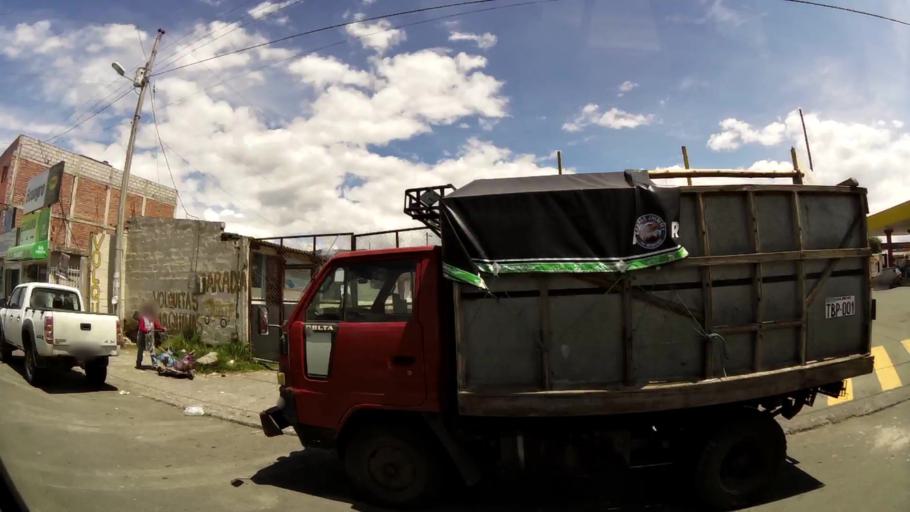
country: EC
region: Chimborazo
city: Riobamba
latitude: -1.6632
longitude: -78.6399
